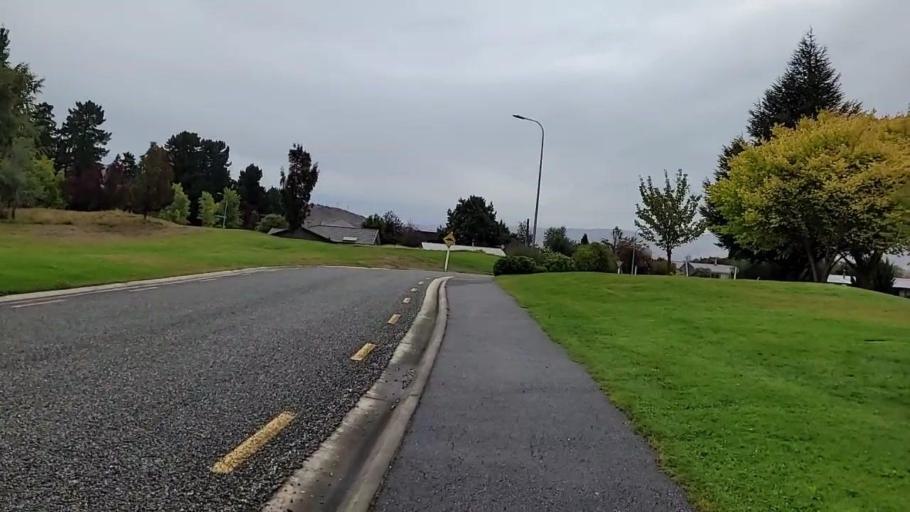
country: NZ
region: Otago
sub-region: Queenstown-Lakes District
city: Wanaka
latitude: -45.0405
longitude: 169.2080
